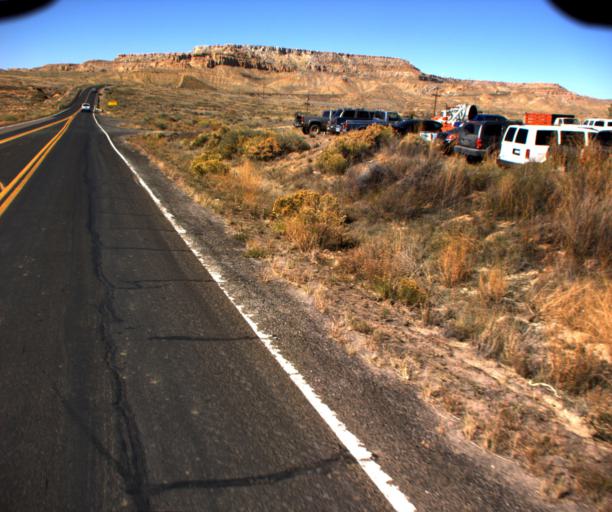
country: US
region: Arizona
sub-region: Navajo County
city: First Mesa
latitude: 35.7934
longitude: -110.5057
